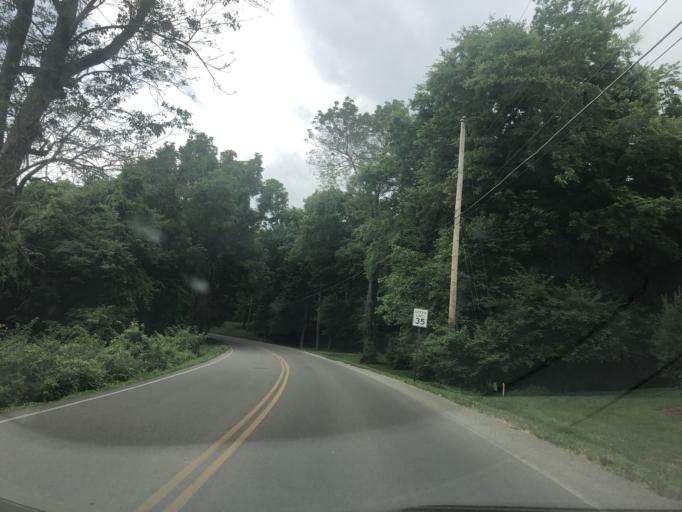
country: US
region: Tennessee
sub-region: Davidson County
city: Forest Hills
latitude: 36.0789
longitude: -86.8233
